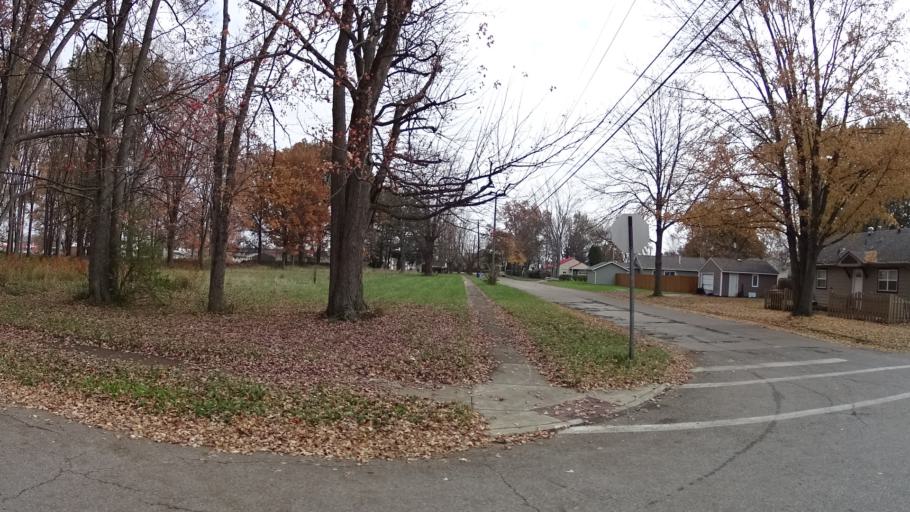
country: US
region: Ohio
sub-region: Lorain County
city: Elyria
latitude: 41.3615
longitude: -82.0805
